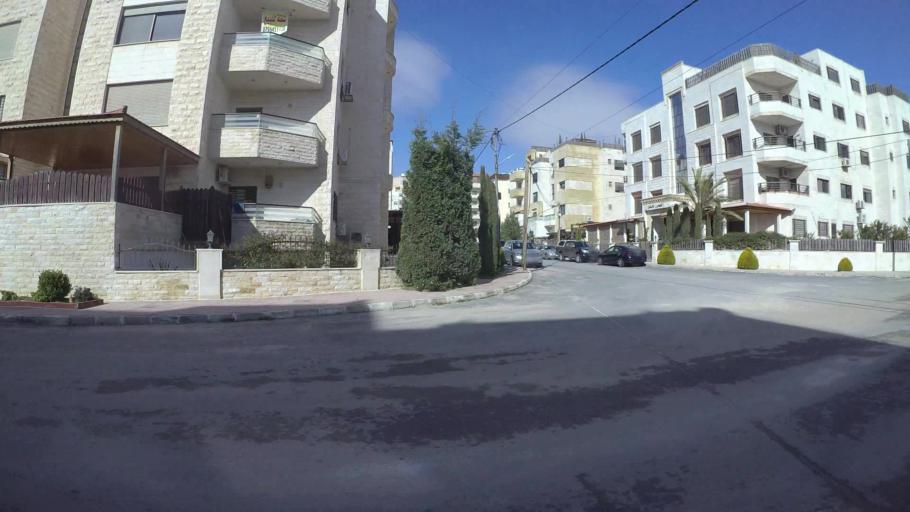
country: JO
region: Amman
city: Al Jubayhah
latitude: 32.0022
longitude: 35.8468
